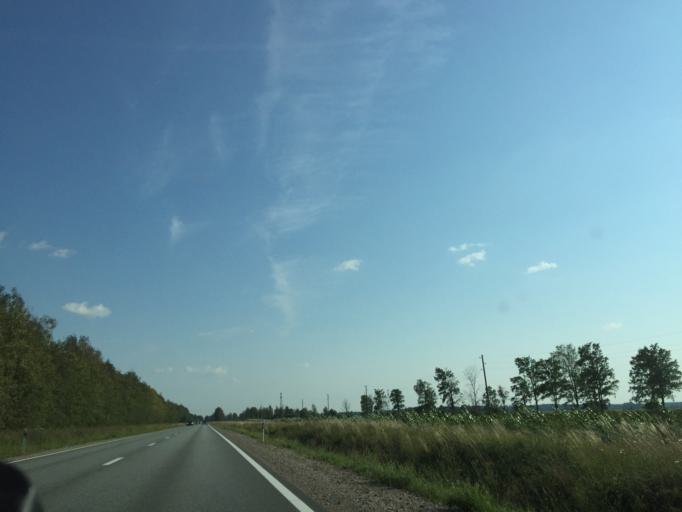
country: LV
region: Jelgava
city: Jelgava
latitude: 56.4437
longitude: 23.6889
